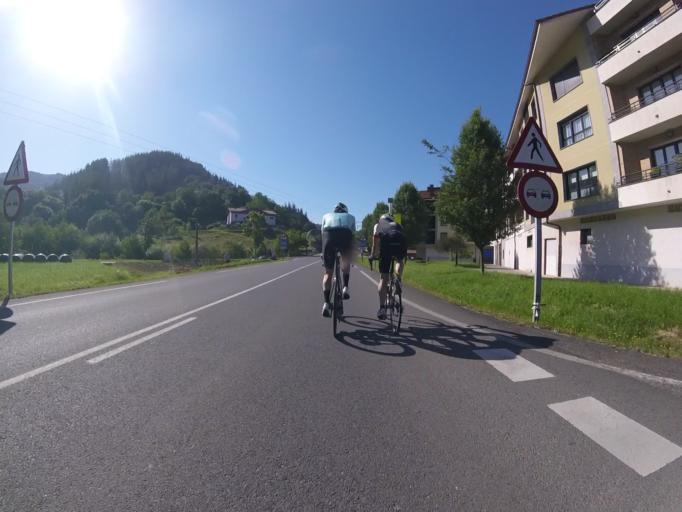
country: ES
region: Basque Country
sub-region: Provincia de Guipuzcoa
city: Azpeitia
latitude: 43.1592
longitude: -2.2446
